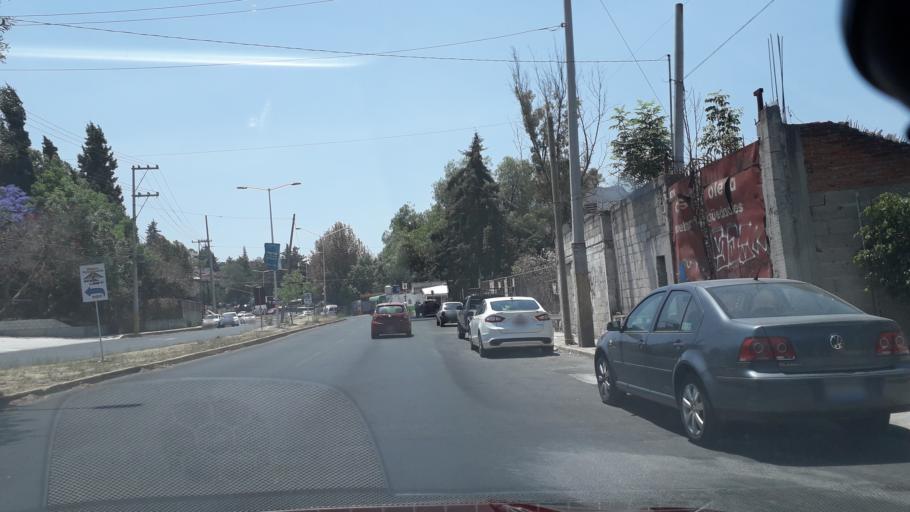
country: MX
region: Puebla
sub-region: Puebla
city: Galaxia la Calera
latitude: 19.0078
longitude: -98.1802
